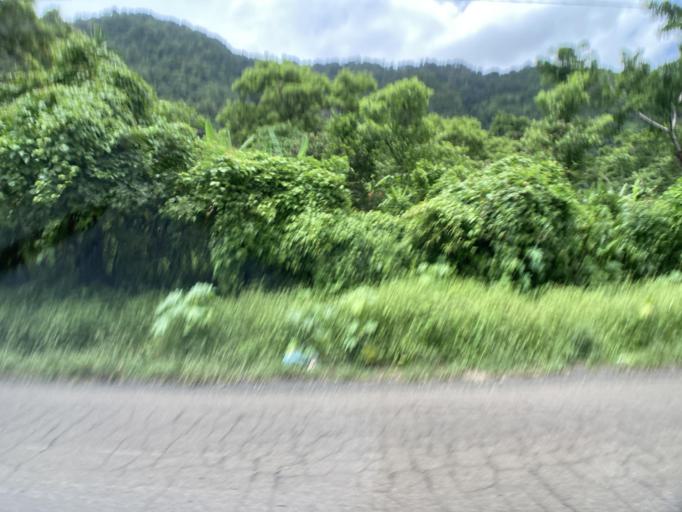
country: GT
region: Guatemala
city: Villa Canales
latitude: 14.4193
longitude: -90.5432
